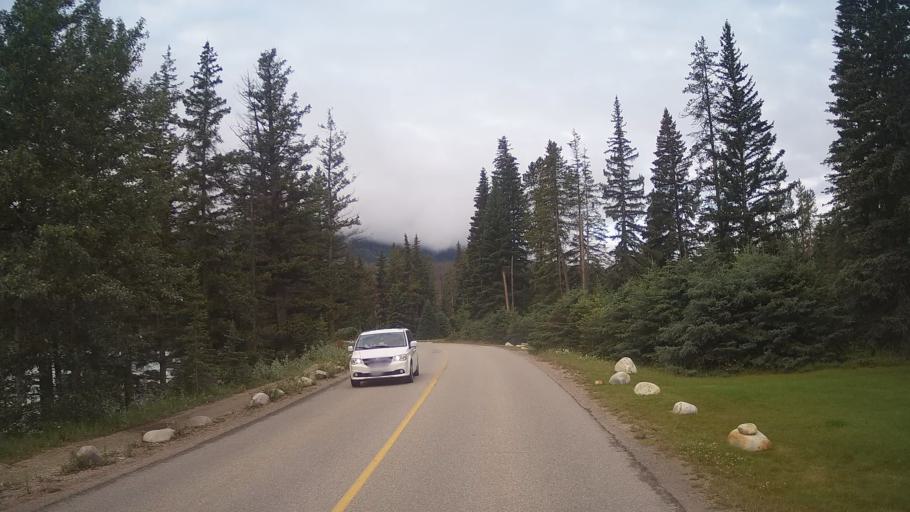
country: CA
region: Alberta
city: Jasper Park Lodge
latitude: 52.8601
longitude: -118.0746
